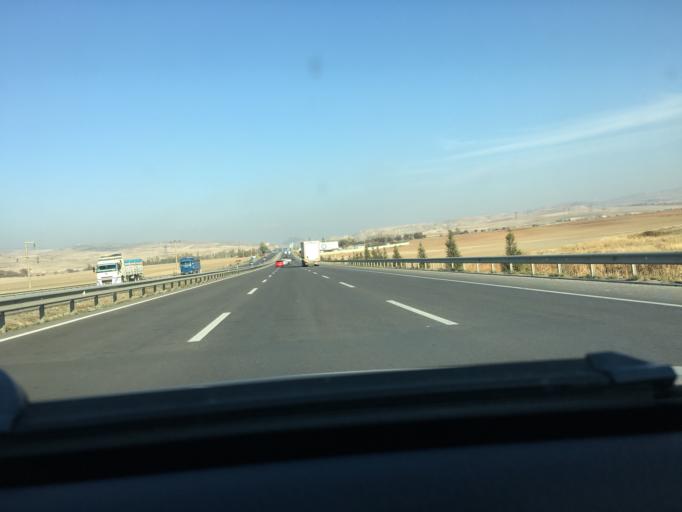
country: TR
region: Ankara
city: Temelli
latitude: 39.7497
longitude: 32.4301
